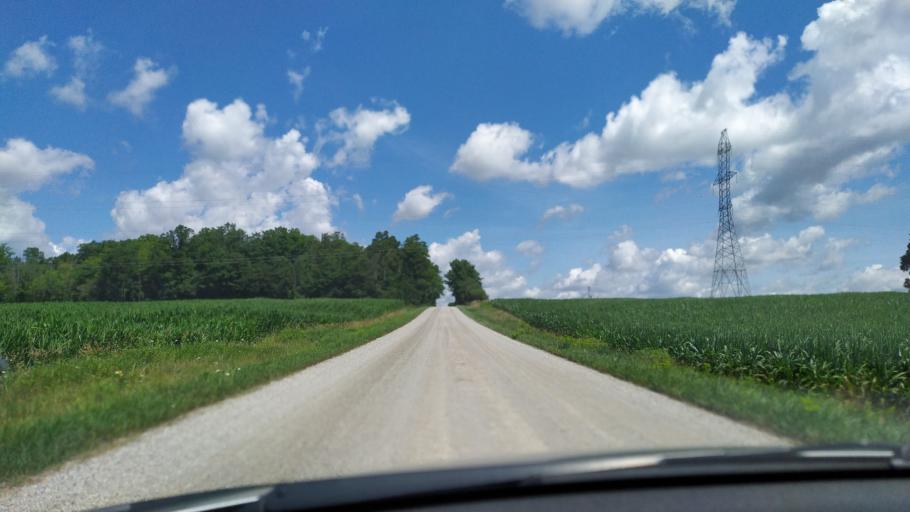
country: CA
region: Ontario
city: Stratford
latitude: 43.3768
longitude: -80.7617
